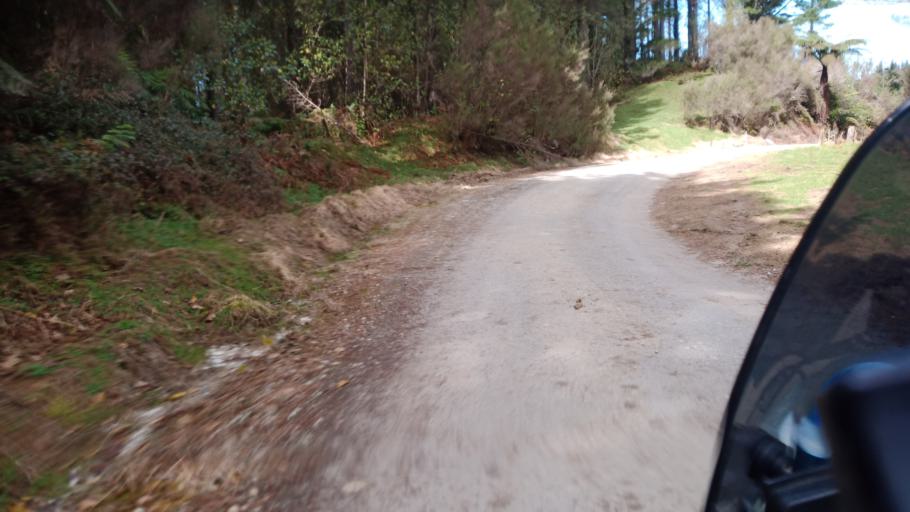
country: NZ
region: Gisborne
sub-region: Gisborne District
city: Gisborne
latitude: -38.8583
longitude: 177.7966
